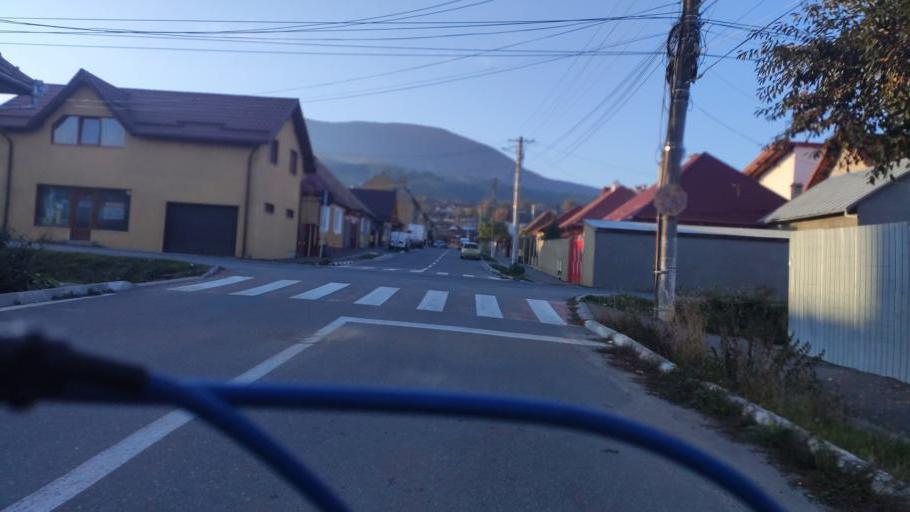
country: RO
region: Brasov
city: Codlea
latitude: 45.6905
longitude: 25.4427
